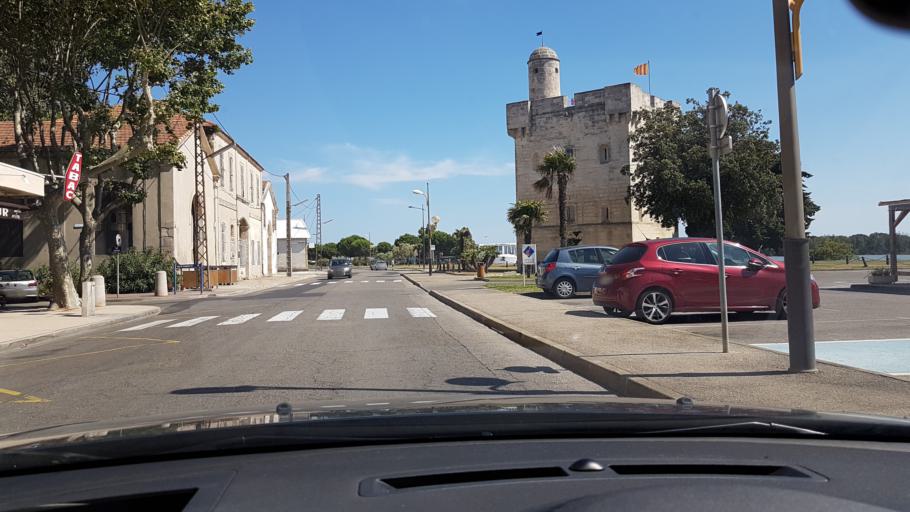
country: FR
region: Provence-Alpes-Cote d'Azur
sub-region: Departement des Bouches-du-Rhone
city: Port-Saint-Louis-du-Rhone
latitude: 43.3853
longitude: 4.8046
